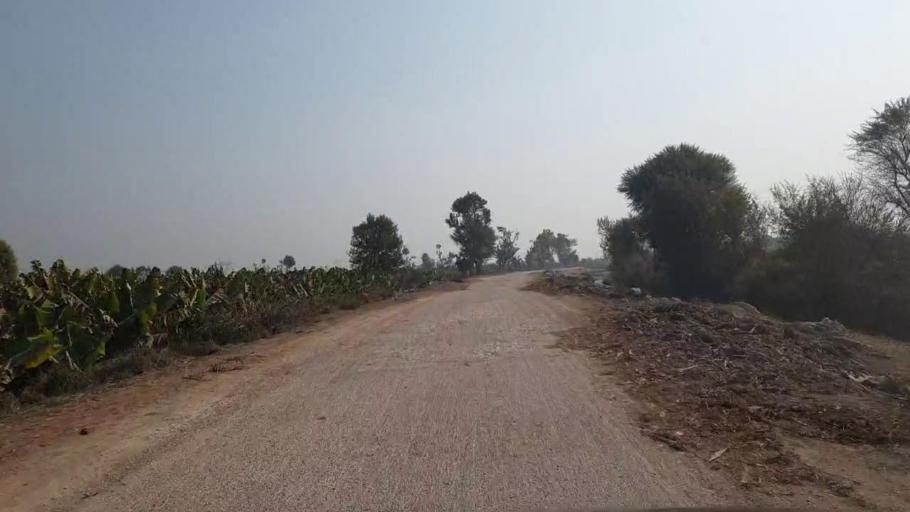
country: PK
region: Sindh
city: Hala
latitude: 25.9587
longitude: 68.4178
